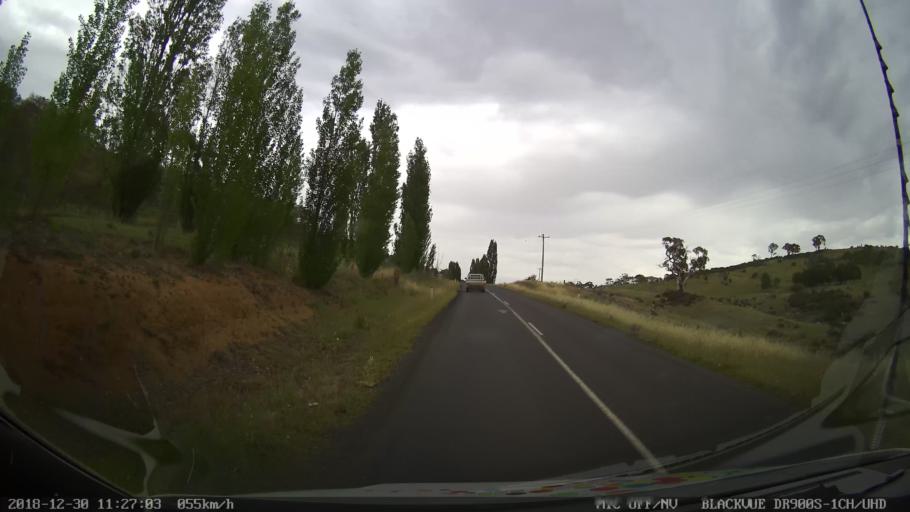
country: AU
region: New South Wales
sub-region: Snowy River
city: Jindabyne
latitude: -36.4634
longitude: 148.6292
